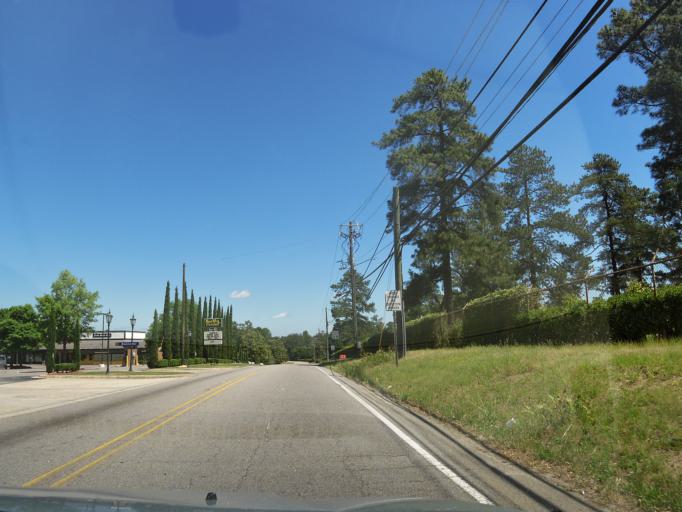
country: US
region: Georgia
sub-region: Columbia County
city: Martinez
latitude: 33.4852
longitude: -82.0299
